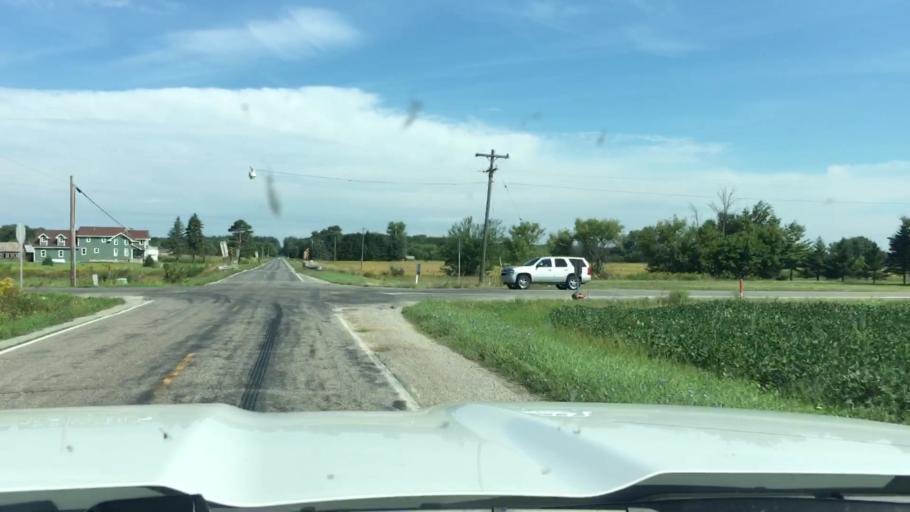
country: US
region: Michigan
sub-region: Saginaw County
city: Hemlock
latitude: 43.4503
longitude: -84.2302
